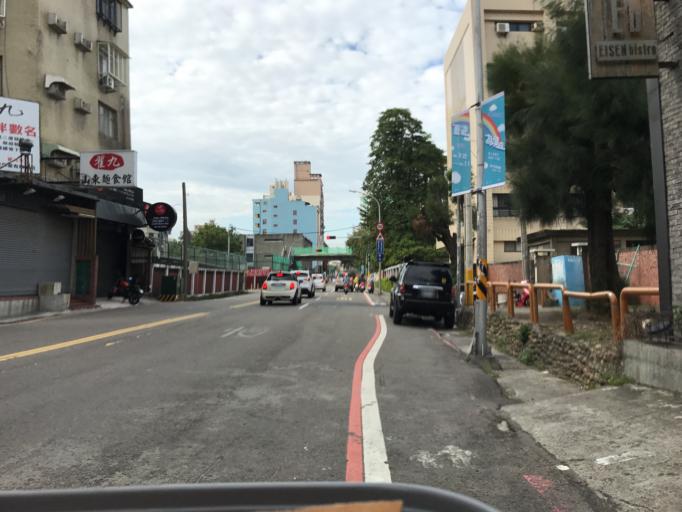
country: TW
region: Taiwan
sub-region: Hsinchu
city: Hsinchu
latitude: 24.8105
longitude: 120.9733
